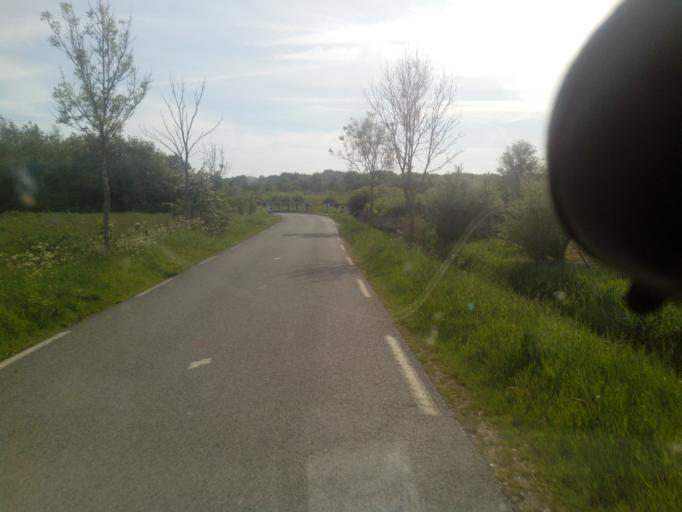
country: FR
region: Nord-Pas-de-Calais
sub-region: Departement du Nord
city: Renescure
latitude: 50.7742
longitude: 2.3601
